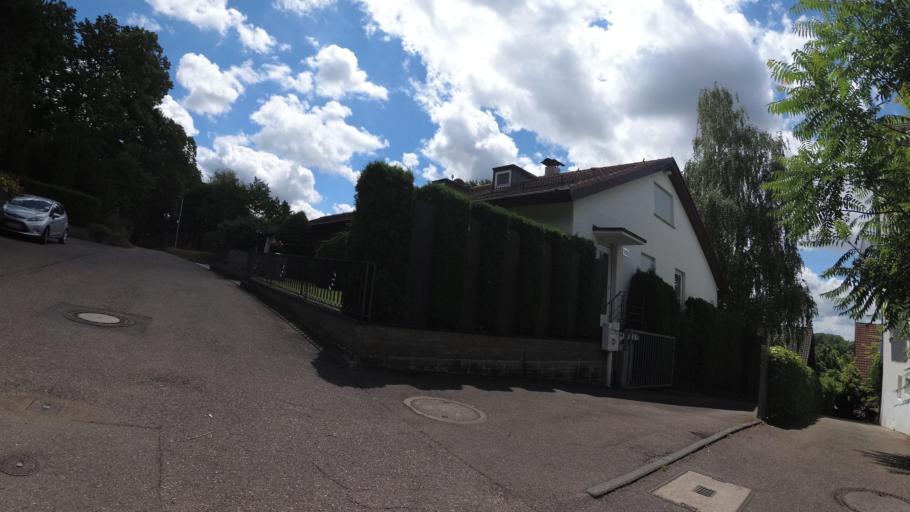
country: DE
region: Baden-Wuerttemberg
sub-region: Regierungsbezirk Stuttgart
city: Heilbronn
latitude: 49.1428
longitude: 9.2435
